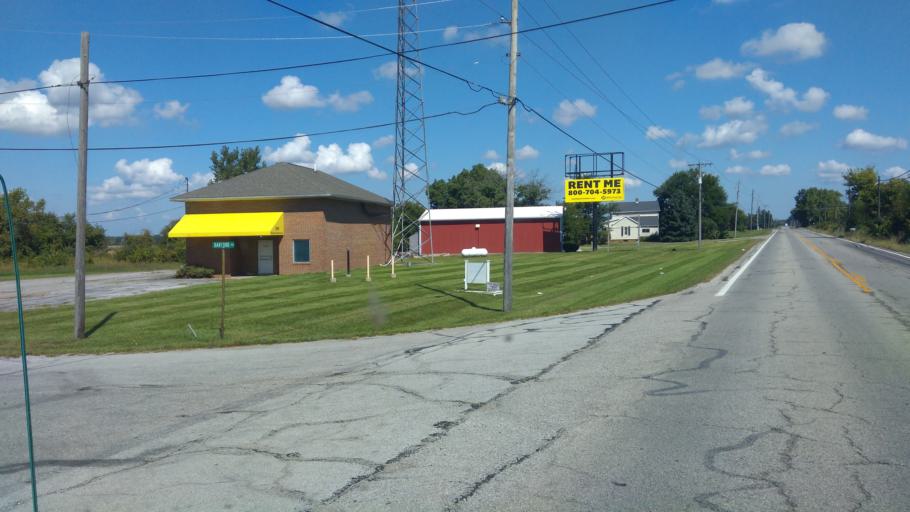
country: US
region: Ohio
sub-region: Marion County
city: Marion
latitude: 40.6269
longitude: -83.1299
